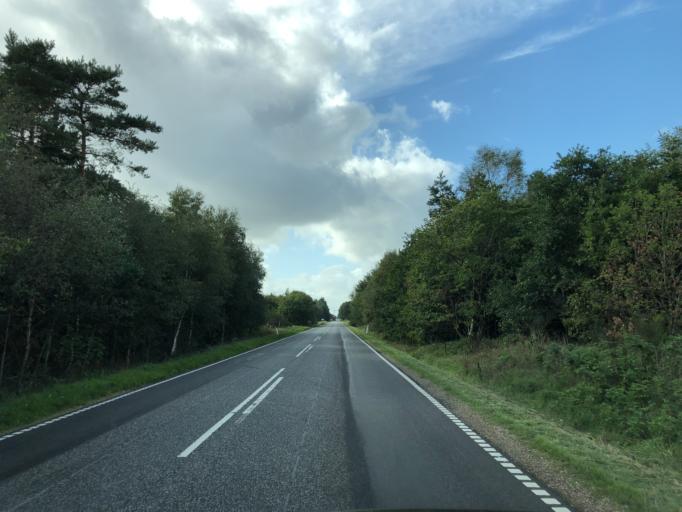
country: DK
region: Central Jutland
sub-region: Holstebro Kommune
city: Holstebro
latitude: 56.3694
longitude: 8.5640
